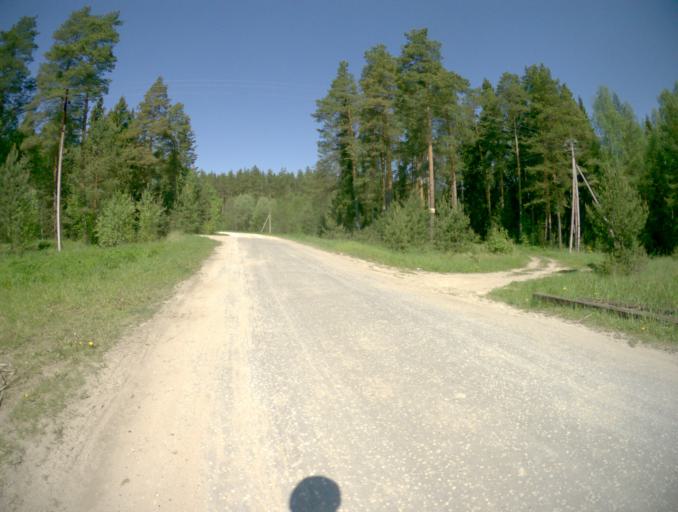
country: RU
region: Vladimir
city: Anopino
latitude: 55.7076
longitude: 40.6604
